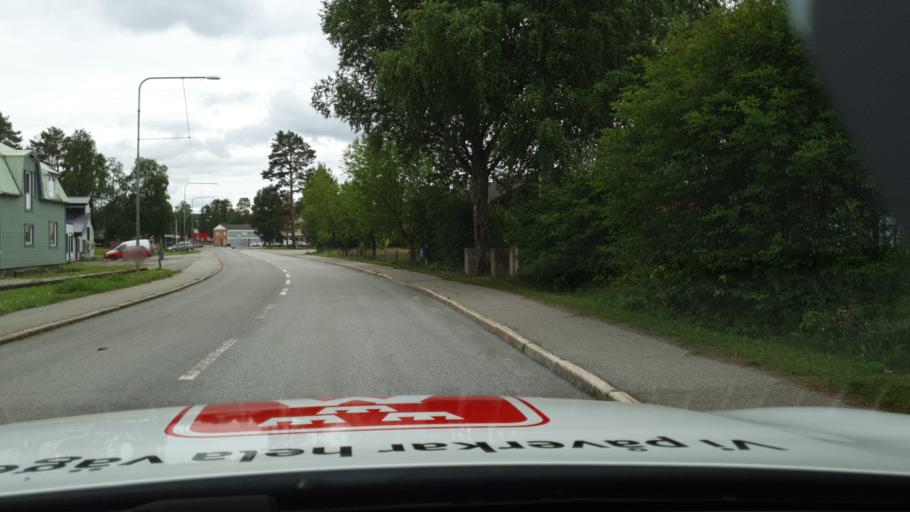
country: SE
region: Vaesterbotten
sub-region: Dorotea Kommun
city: Dorotea
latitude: 64.1188
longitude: 16.2054
